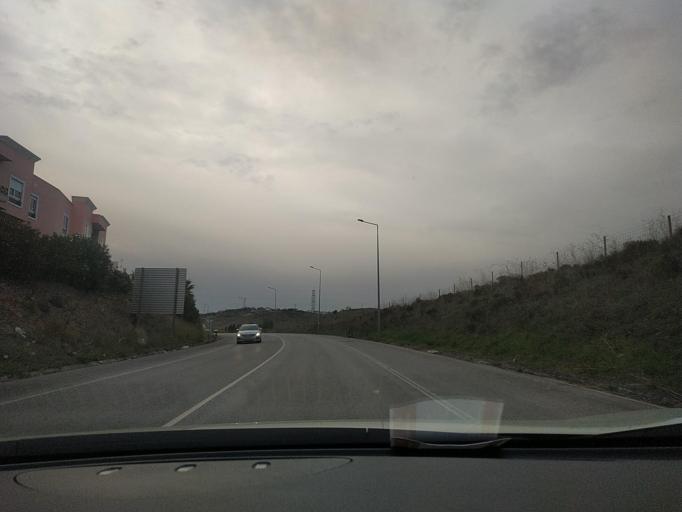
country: PT
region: Lisbon
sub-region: Loures
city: Santa Iria da Azoia
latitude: 38.8629
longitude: -9.1022
